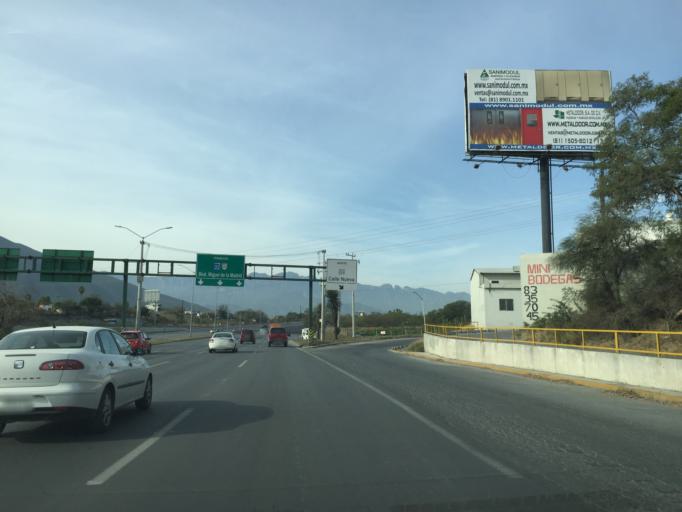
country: MX
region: Nuevo Leon
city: Guadalupe
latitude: 25.6919
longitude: -100.2165
